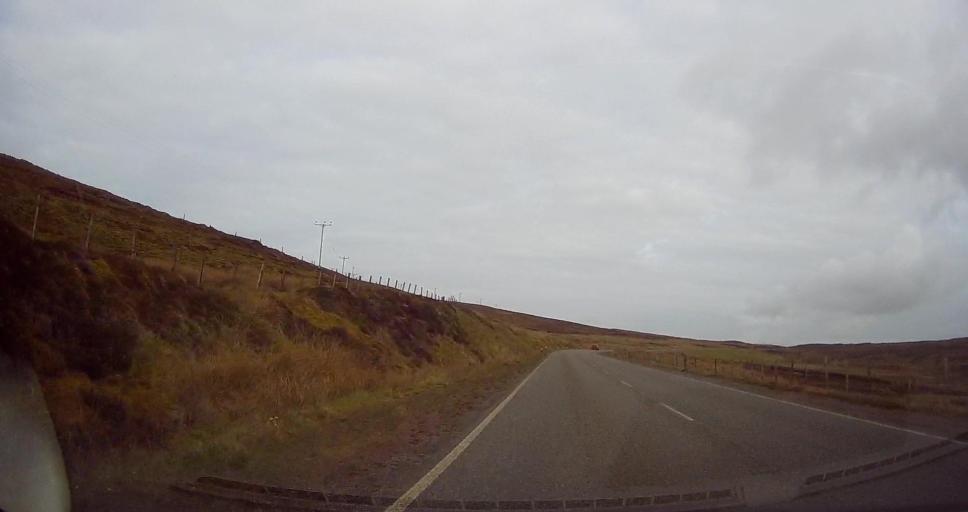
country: GB
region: Scotland
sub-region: Shetland Islands
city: Sandwick
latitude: 60.0831
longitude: -1.2314
